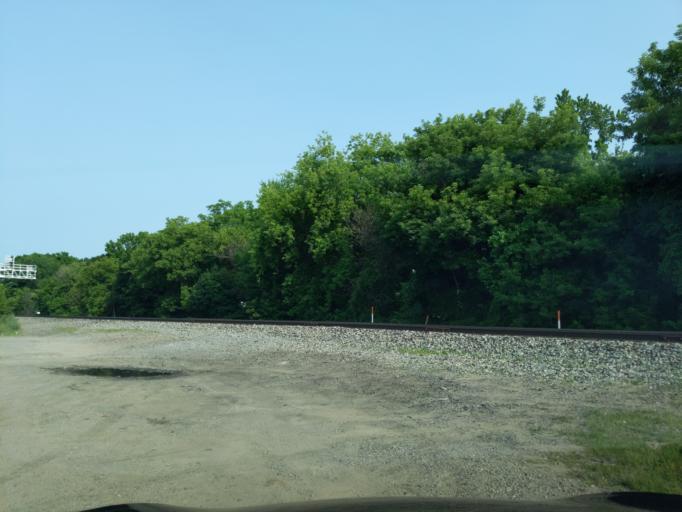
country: US
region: Michigan
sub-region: Ingham County
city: Lansing
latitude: 42.7194
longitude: -84.5416
